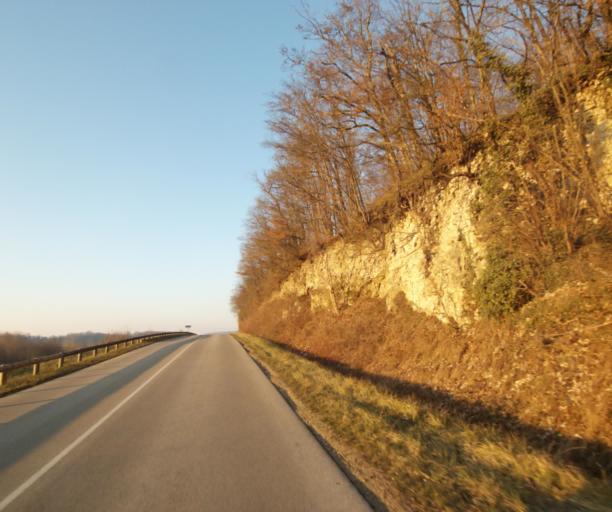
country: FR
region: Champagne-Ardenne
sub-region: Departement de la Haute-Marne
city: Bienville
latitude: 48.5891
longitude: 5.0431
